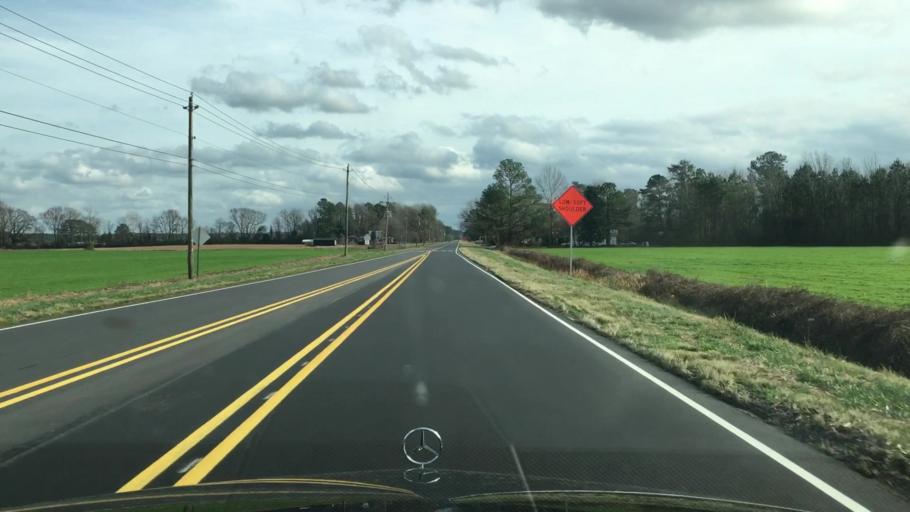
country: US
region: North Carolina
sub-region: Duplin County
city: Warsaw
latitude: 34.9832
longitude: -78.0379
